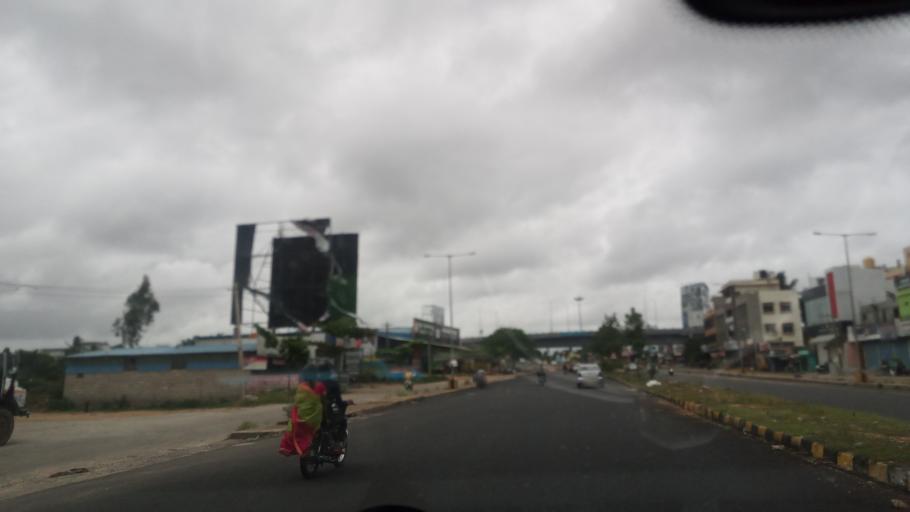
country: IN
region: Karnataka
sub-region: Mysore
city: Mysore
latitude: 12.3312
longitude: 76.5980
